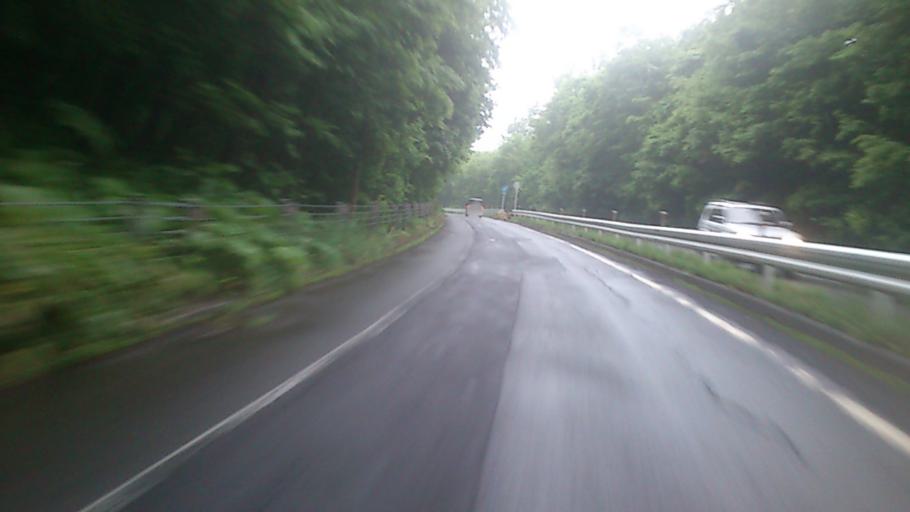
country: JP
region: Hokkaido
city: Chitose
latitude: 42.8030
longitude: 141.5733
